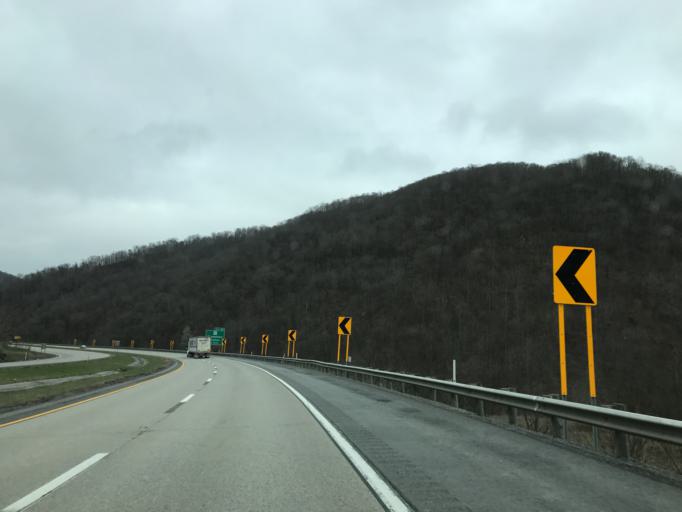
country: US
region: West Virginia
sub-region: Summers County
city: Hinton
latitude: 37.7788
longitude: -80.9300
